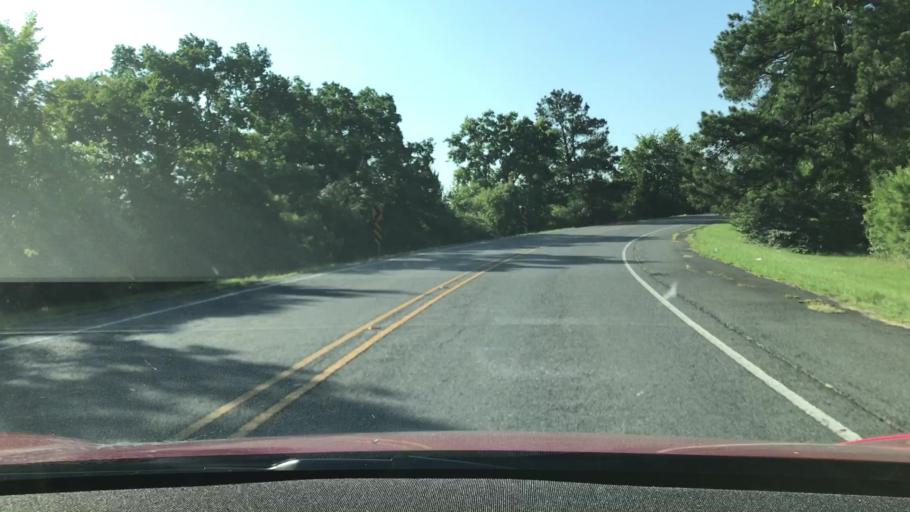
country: US
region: Louisiana
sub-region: Caddo Parish
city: Shreveport
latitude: 32.4535
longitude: -93.8449
